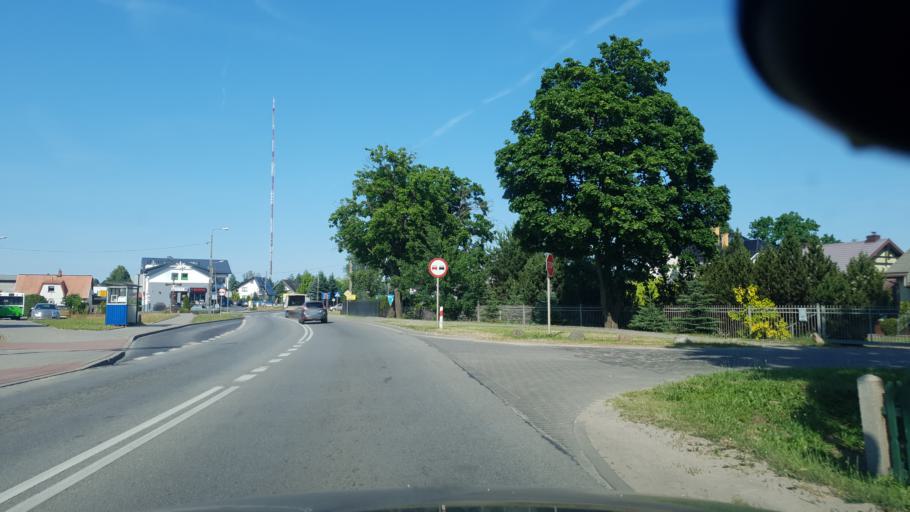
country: PL
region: Pomeranian Voivodeship
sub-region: Powiat kartuski
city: Chwaszczyno
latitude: 54.4458
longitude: 18.4226
